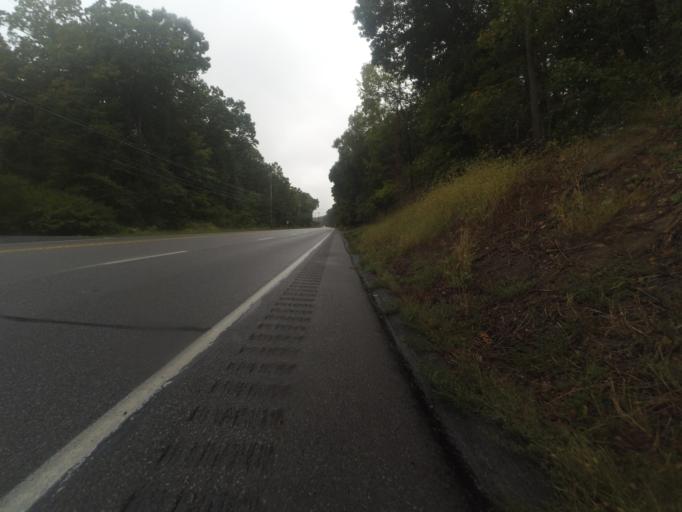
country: US
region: Pennsylvania
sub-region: Huntingdon County
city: Huntingdon
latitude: 40.4961
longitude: -78.0497
